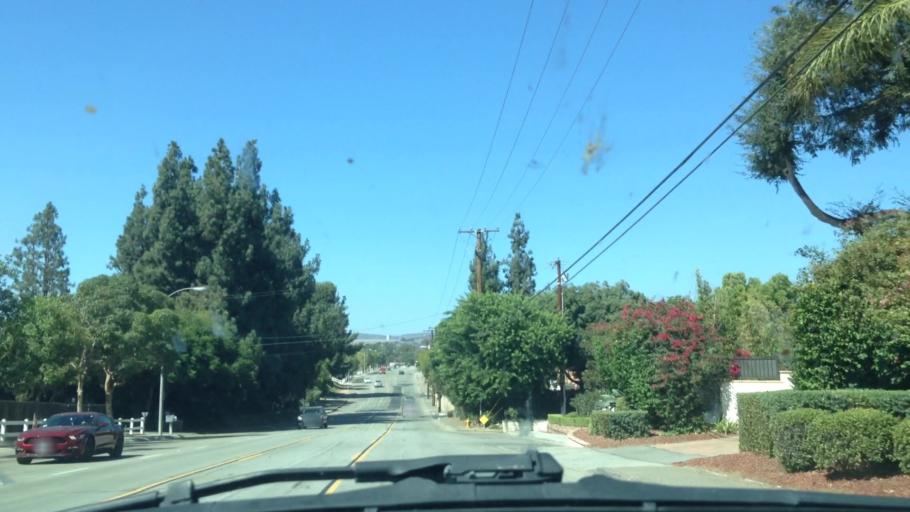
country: US
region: California
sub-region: Orange County
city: Yorba Linda
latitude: 33.8734
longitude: -117.8160
